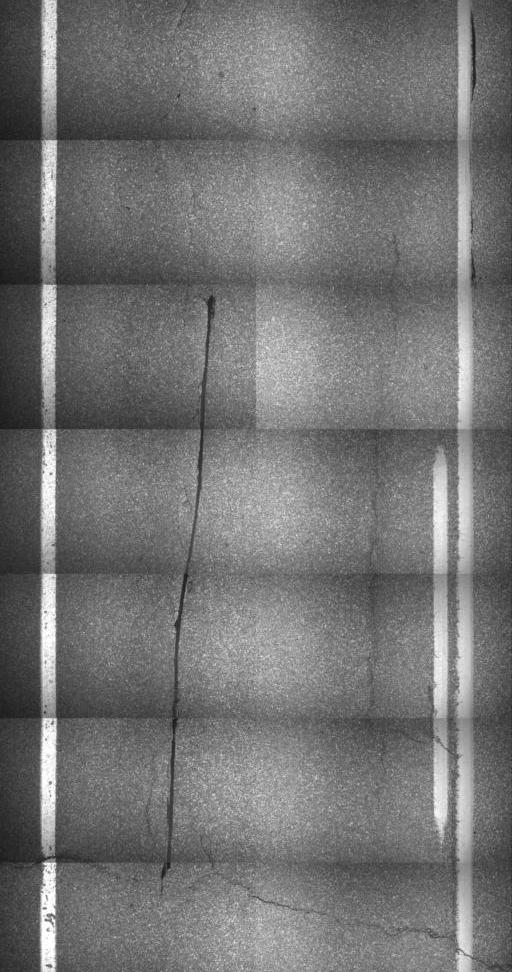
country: US
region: Vermont
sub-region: Lamoille County
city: Johnson
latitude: 44.6030
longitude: -72.8090
